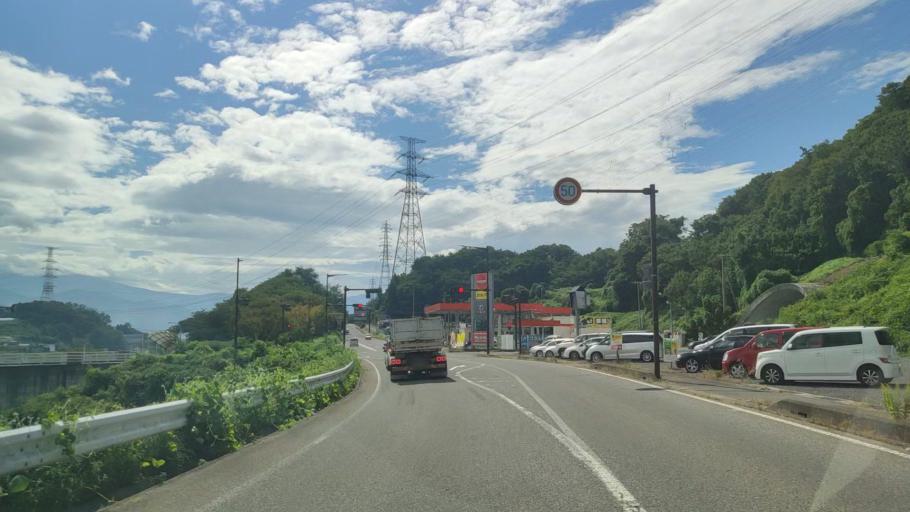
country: JP
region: Nagano
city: Nakano
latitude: 36.7327
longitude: 138.3064
